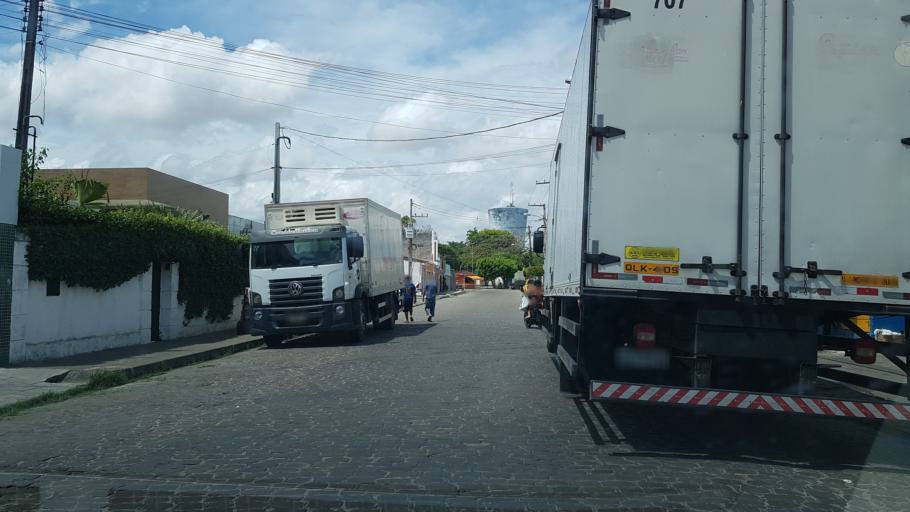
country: BR
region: Alagoas
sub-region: Penedo
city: Penedo
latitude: -10.2813
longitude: -36.5630
